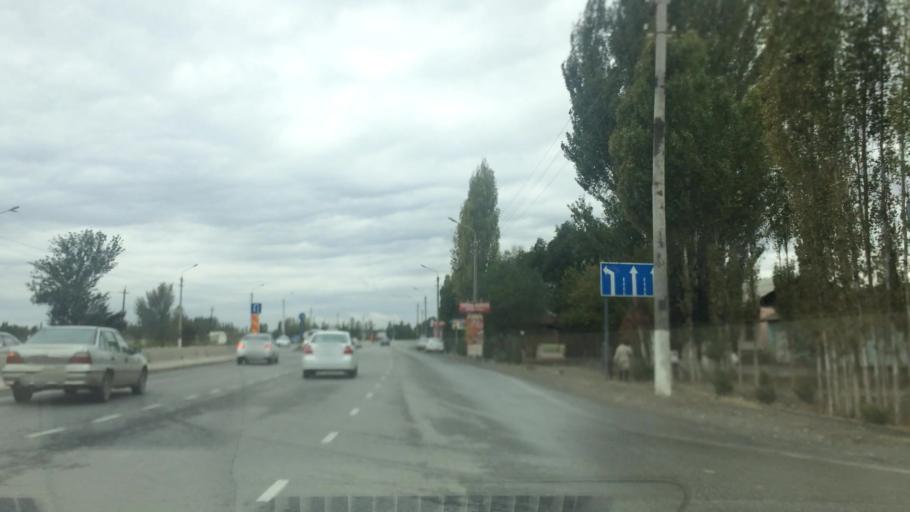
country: UZ
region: Jizzax
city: Jizzax
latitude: 39.9809
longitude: 67.5693
